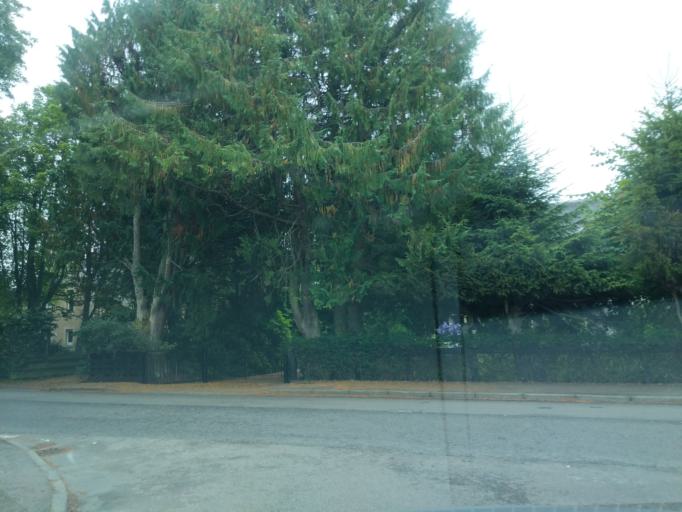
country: GB
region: Scotland
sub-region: Highland
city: Grantown on Spey
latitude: 57.3324
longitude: -3.6124
